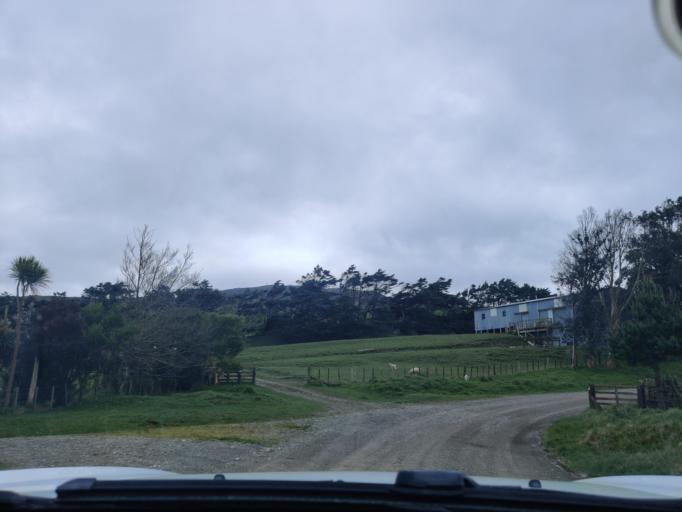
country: NZ
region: Manawatu-Wanganui
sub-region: Palmerston North City
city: Palmerston North
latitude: -40.2866
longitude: 175.8604
